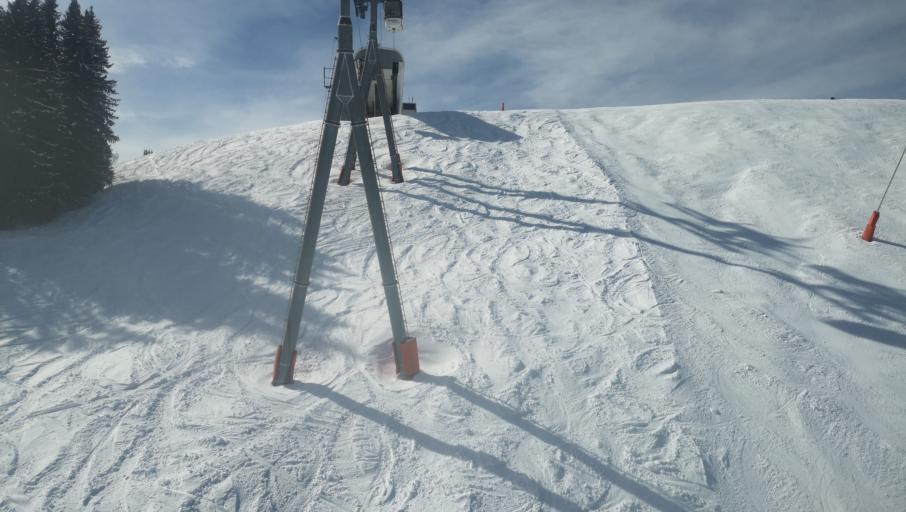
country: FR
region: Rhone-Alpes
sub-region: Departement de la Haute-Savoie
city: Megeve
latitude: 45.8335
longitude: 6.6152
